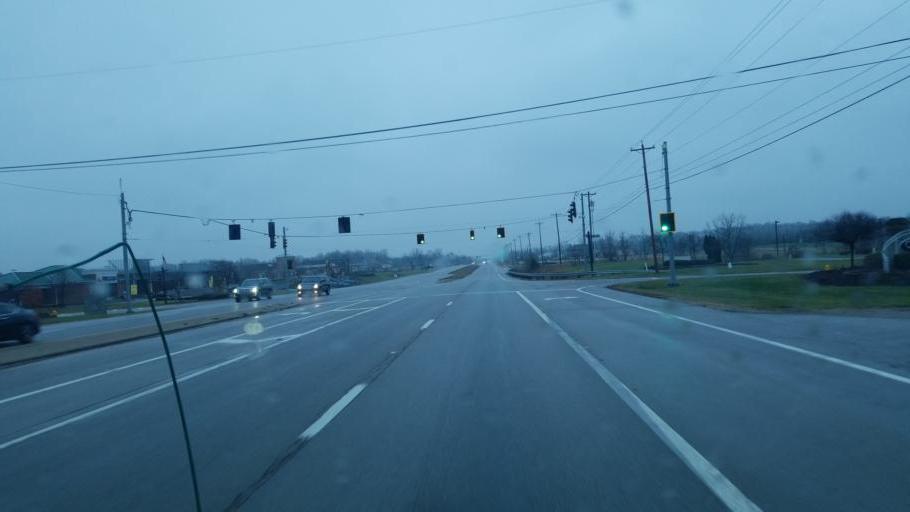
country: US
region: Ohio
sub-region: Delaware County
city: Lewis Center
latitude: 40.2057
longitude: -83.0307
